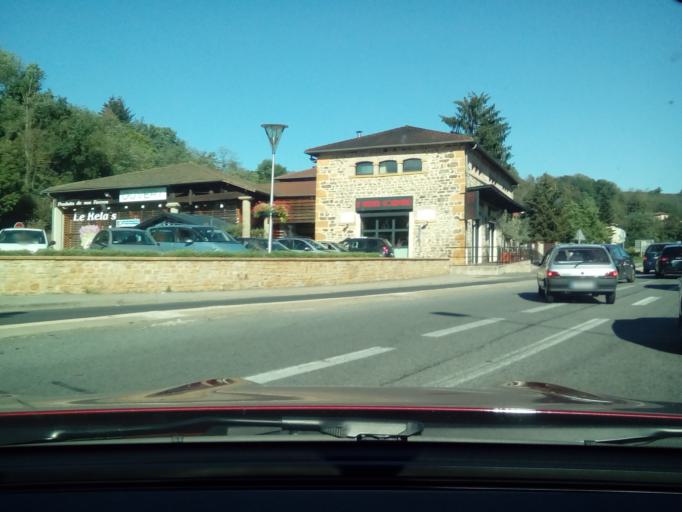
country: FR
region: Rhone-Alpes
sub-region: Departement du Rhone
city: Saint-Verand
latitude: 45.9070
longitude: 4.5742
